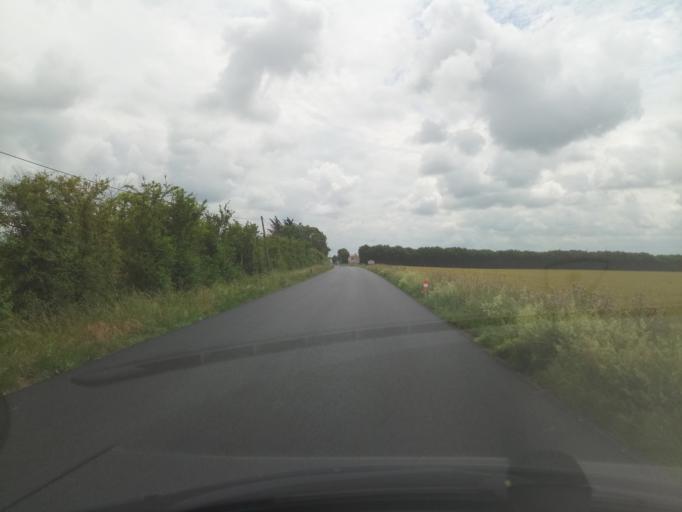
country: FR
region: Poitou-Charentes
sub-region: Departement de la Charente-Maritime
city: Saint-Jean-de-Liversay
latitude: 46.2692
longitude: -0.8866
